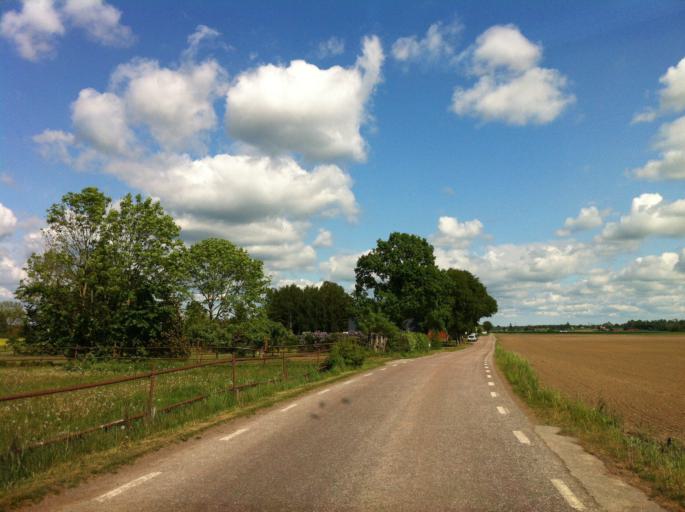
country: SE
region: Skane
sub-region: Landskrona
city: Asmundtorp
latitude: 55.9595
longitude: 12.9068
